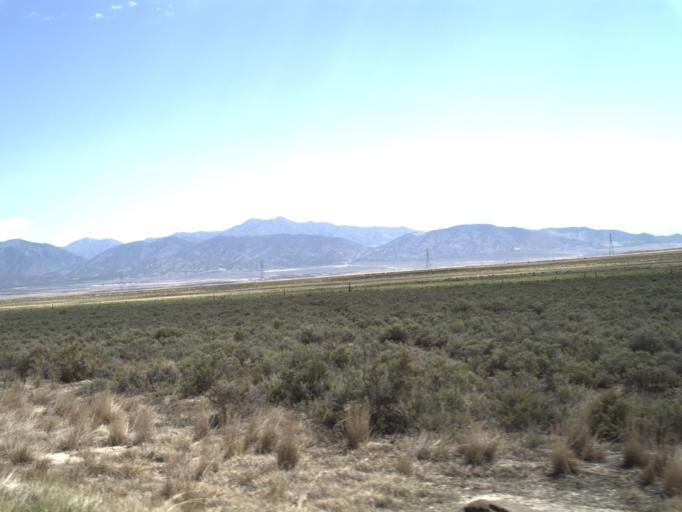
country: US
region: Utah
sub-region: Tooele County
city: Tooele
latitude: 40.2233
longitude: -112.4048
